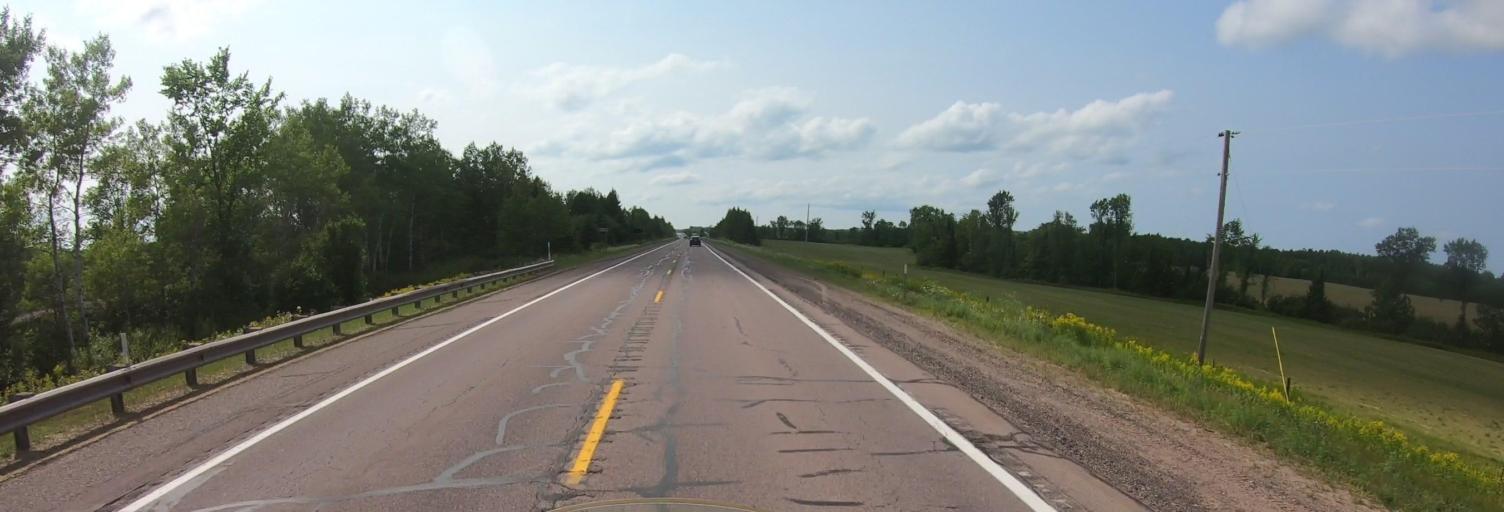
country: US
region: Michigan
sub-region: Ontonagon County
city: Ontonagon
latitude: 46.5715
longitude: -89.4707
